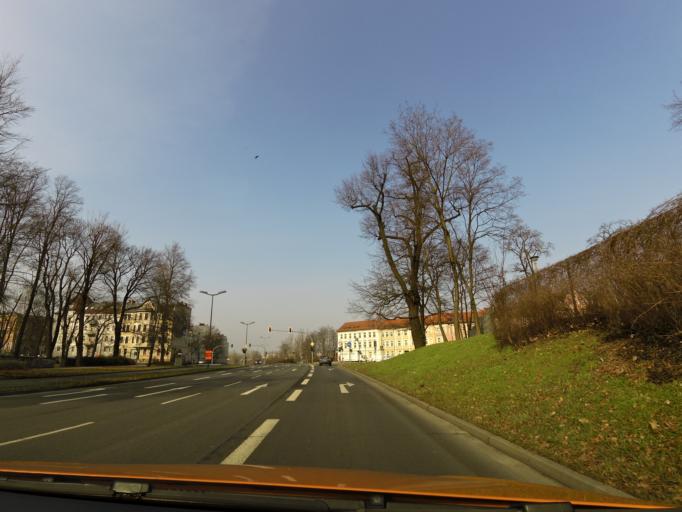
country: DE
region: Brandenburg
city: Frankfurt (Oder)
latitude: 52.3458
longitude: 14.5397
